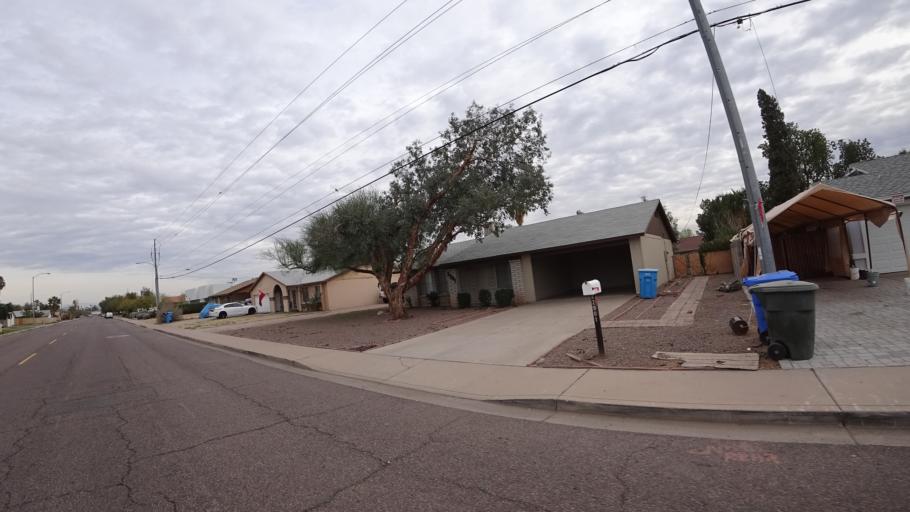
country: US
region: Arizona
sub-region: Maricopa County
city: Glendale
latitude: 33.6473
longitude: -112.1223
